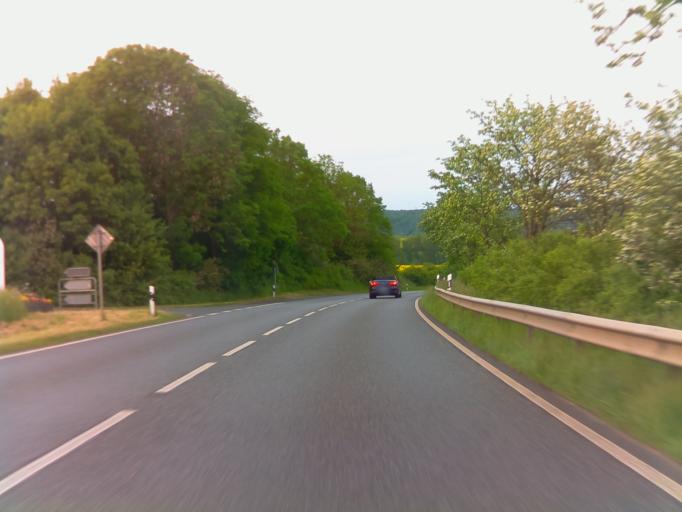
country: DE
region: Hesse
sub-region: Regierungsbezirk Kassel
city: Neuental
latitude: 51.0612
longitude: 9.1872
